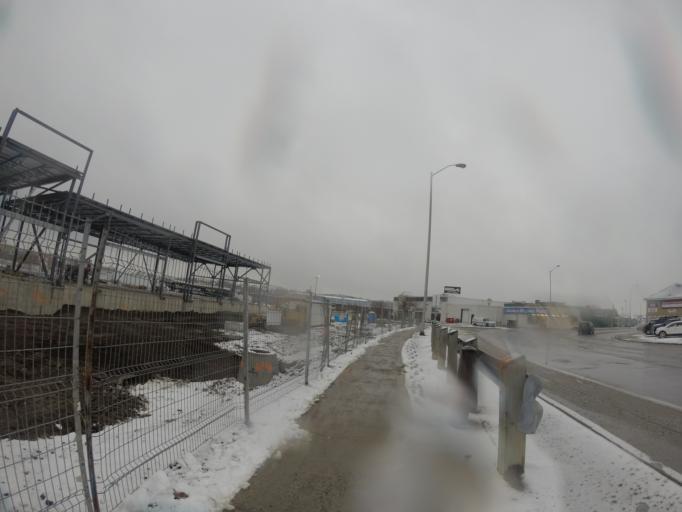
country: CA
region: Ontario
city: Greater Sudbury
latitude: 46.4919
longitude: -81.0005
